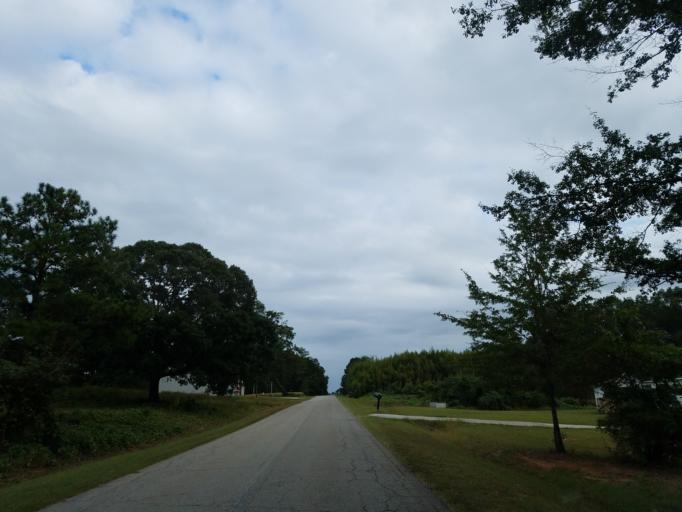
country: US
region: Georgia
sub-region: Lamar County
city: Barnesville
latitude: 33.1614
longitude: -84.0767
